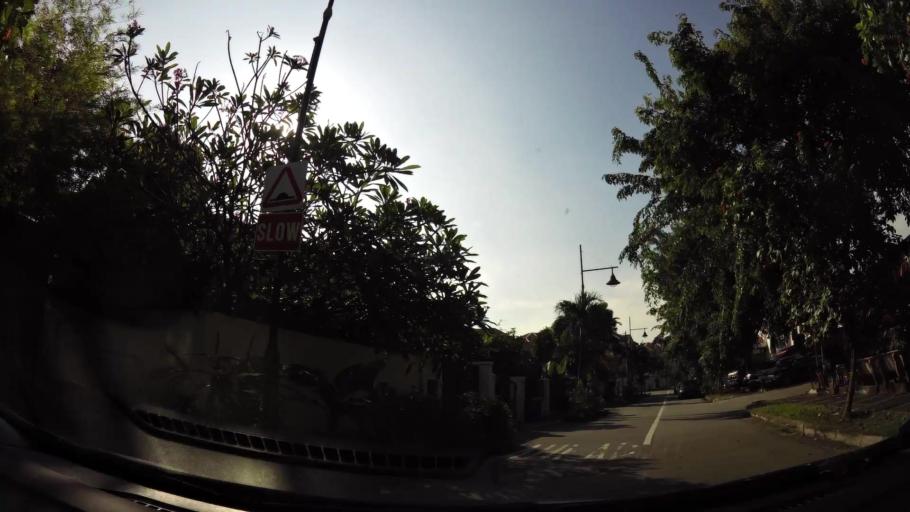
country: SG
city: Singapore
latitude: 1.3163
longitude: 103.9256
